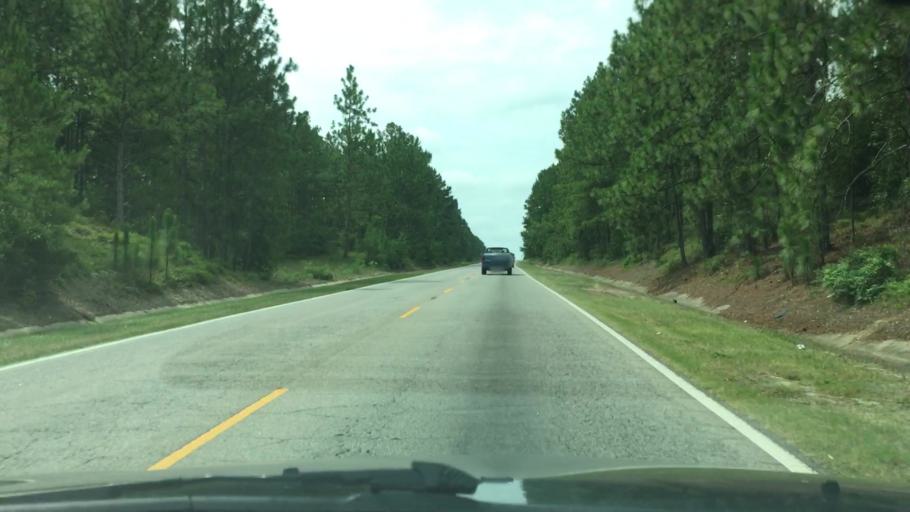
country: US
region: South Carolina
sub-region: Aiken County
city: Warrenville
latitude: 33.5511
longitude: -81.7777
